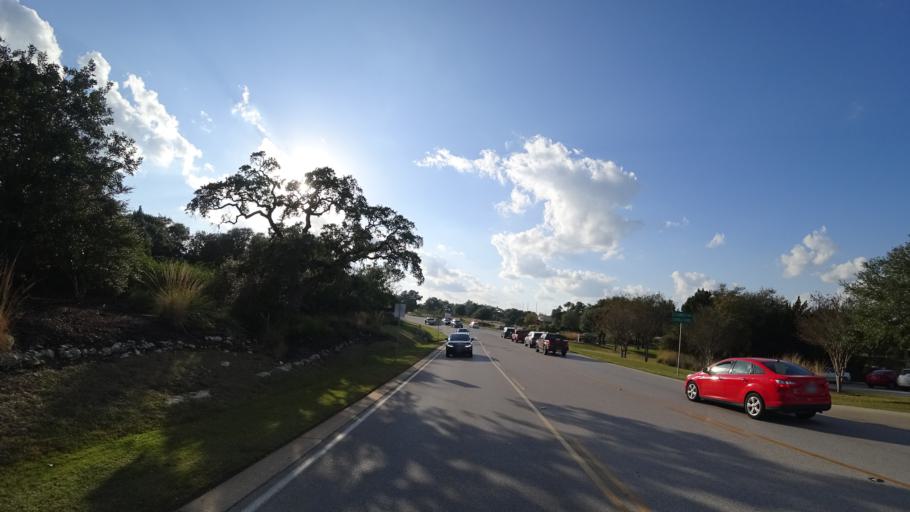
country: US
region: Texas
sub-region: Travis County
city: Barton Creek
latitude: 30.2888
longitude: -97.8717
